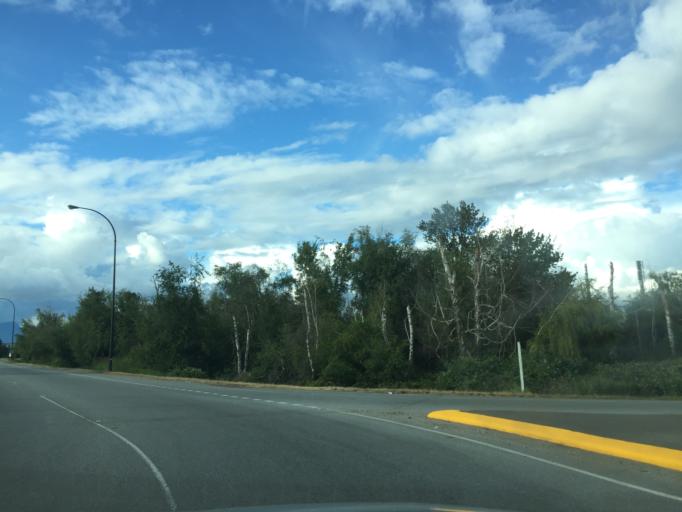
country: CA
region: British Columbia
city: Richmond
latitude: 49.1702
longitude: -123.0745
